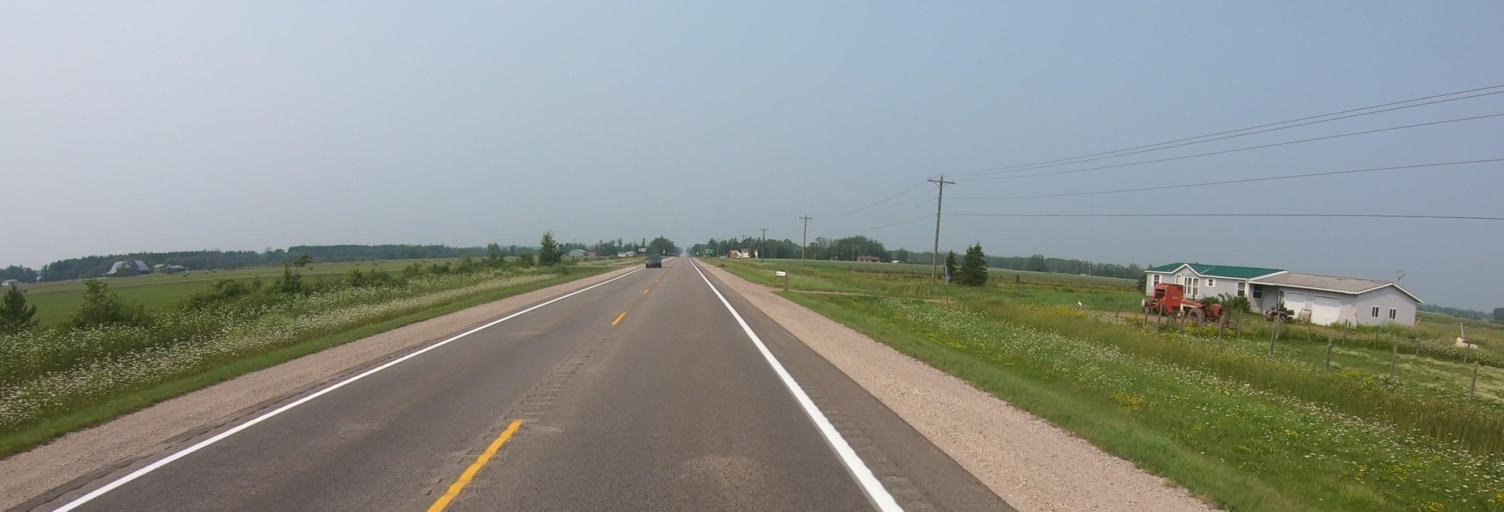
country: US
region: Michigan
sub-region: Chippewa County
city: Sault Ste. Marie
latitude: 46.1824
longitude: -84.3635
